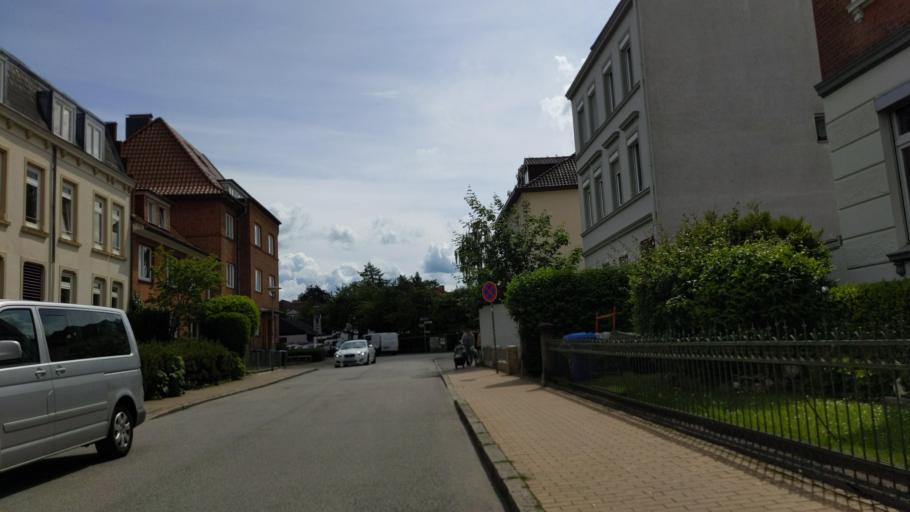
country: DE
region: Schleswig-Holstein
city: Luebeck
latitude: 53.8606
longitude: 10.7000
